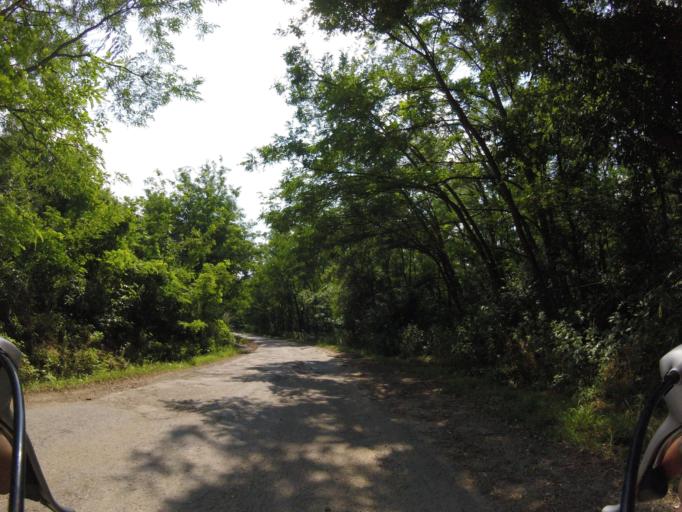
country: SK
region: Nitriansky
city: Sahy
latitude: 47.9999
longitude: 18.8209
